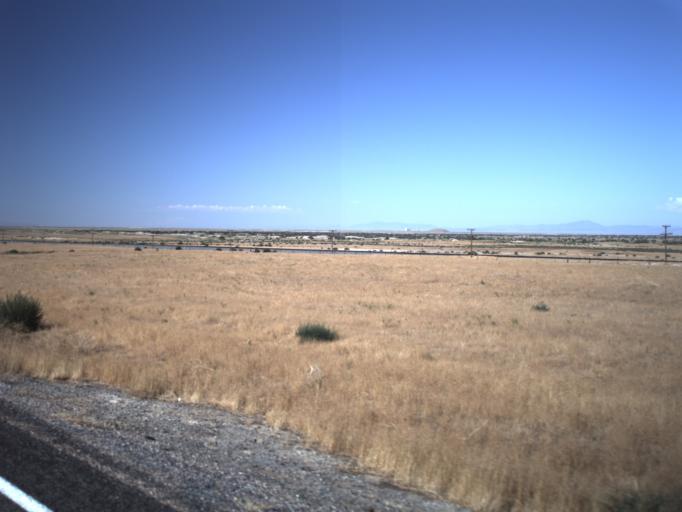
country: US
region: Utah
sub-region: Millard County
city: Delta
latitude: 39.6098
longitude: -112.3203
